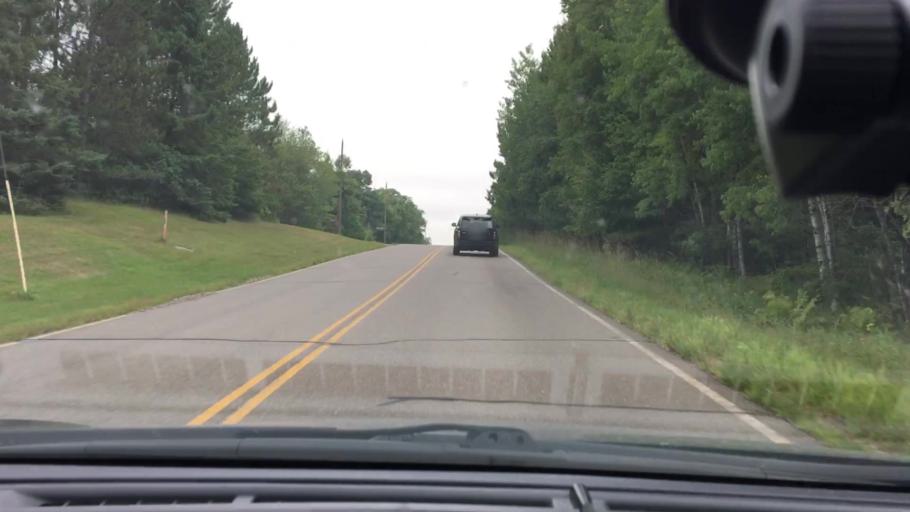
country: US
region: Minnesota
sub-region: Crow Wing County
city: Cross Lake
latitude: 46.6483
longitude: -94.0095
